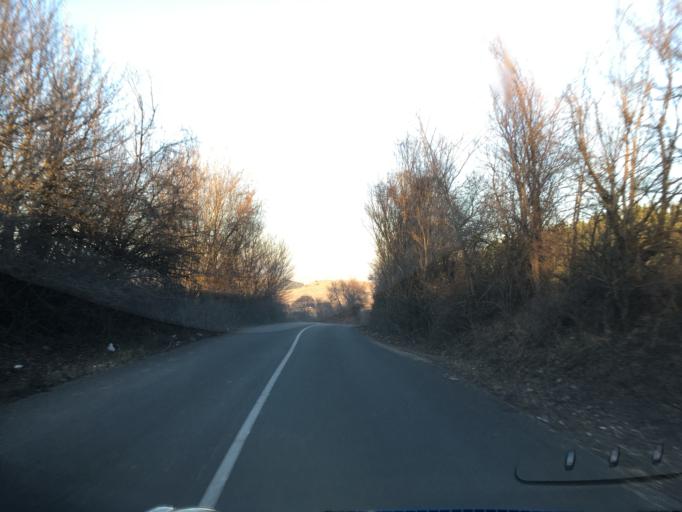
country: GR
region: West Macedonia
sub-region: Nomos Kozanis
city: Koila
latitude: 40.3255
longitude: 21.7996
